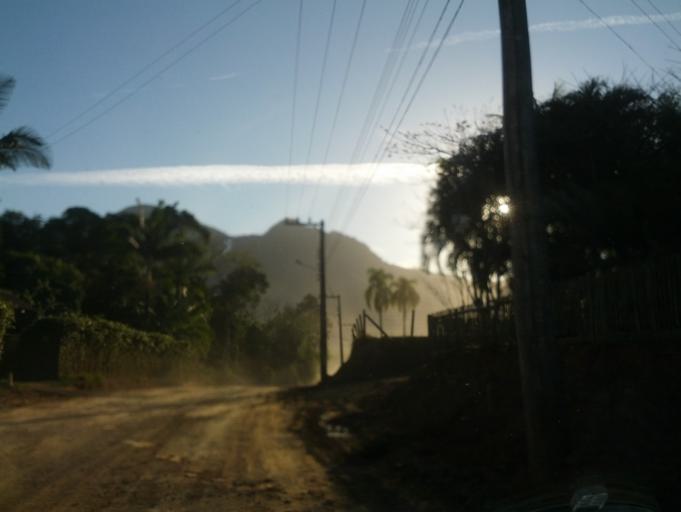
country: BR
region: Santa Catarina
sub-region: Indaial
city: Indaial
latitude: -26.9100
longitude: -49.2675
